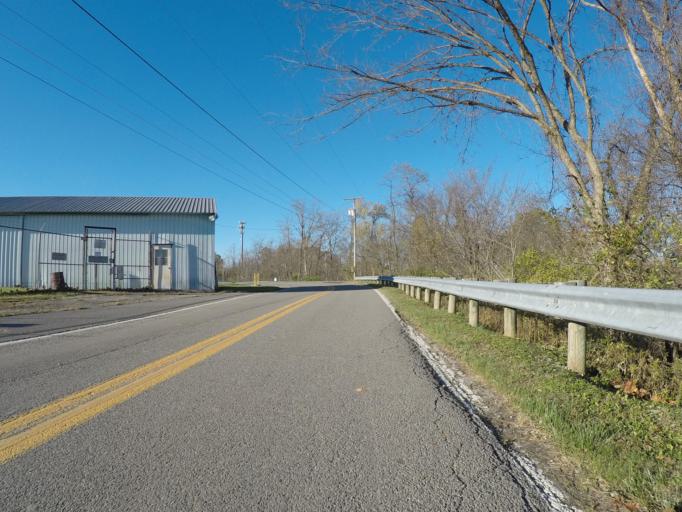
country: US
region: West Virginia
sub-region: Wayne County
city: Ceredo
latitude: 38.3732
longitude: -82.5594
